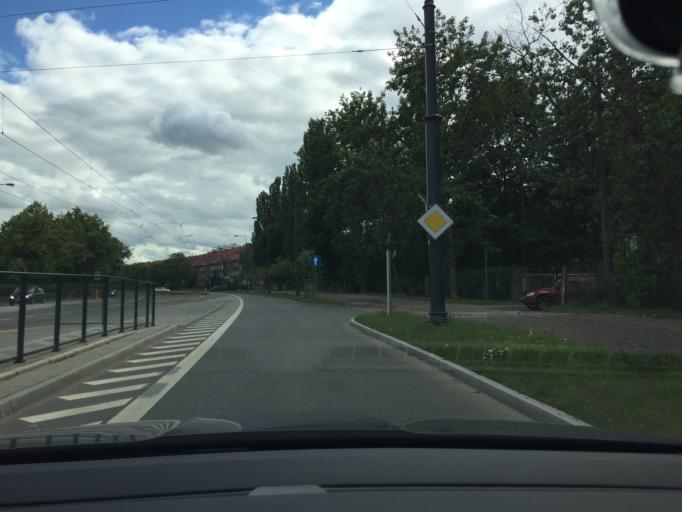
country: PL
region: Pomeranian Voivodeship
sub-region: Gdansk
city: Gdansk
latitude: 54.3523
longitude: 18.6716
